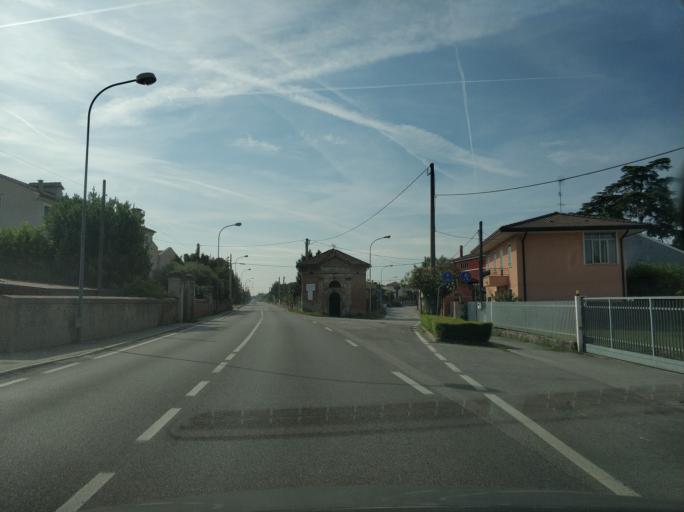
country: IT
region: Veneto
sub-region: Provincia di Padova
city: Este
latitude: 45.2190
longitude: 11.6646
